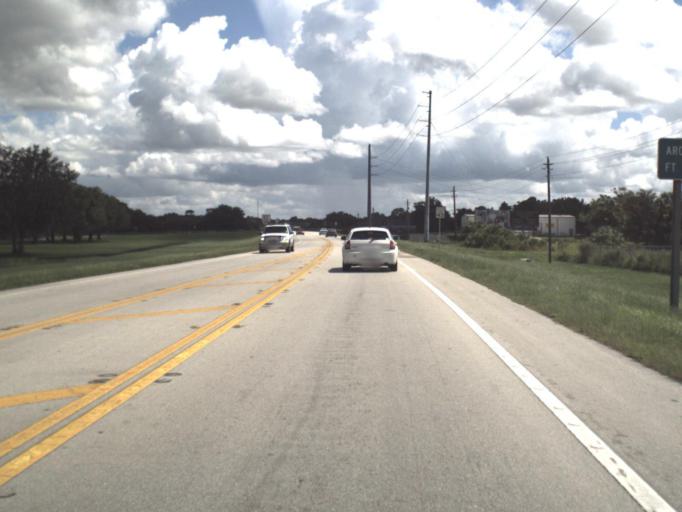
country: US
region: Florida
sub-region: DeSoto County
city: Arcadia
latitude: 27.2250
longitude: -81.8875
